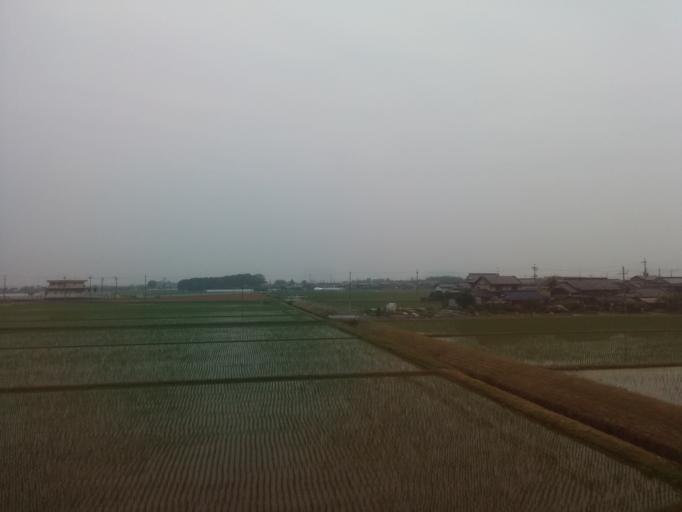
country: JP
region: Shiga Prefecture
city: Omihachiman
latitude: 35.0933
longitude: 136.0613
